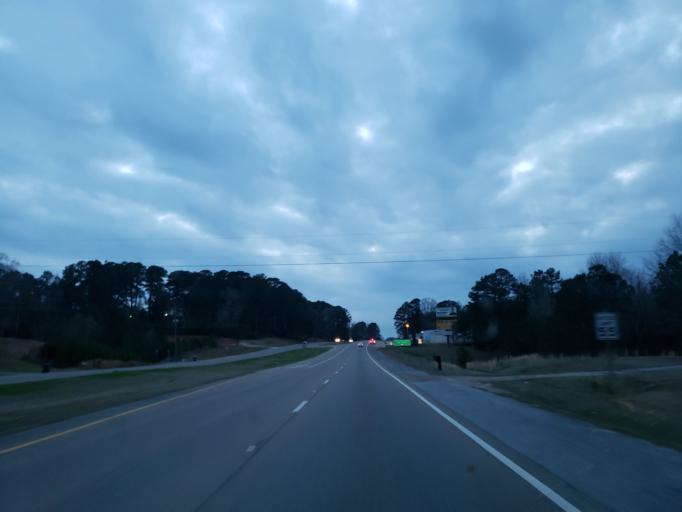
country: US
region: Mississippi
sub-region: Lauderdale County
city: Marion
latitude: 32.3674
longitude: -88.6400
